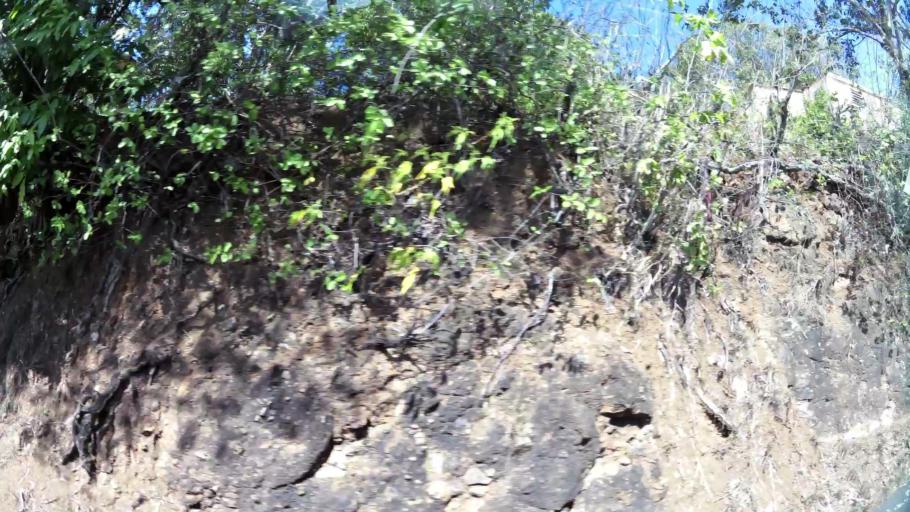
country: VG
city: Tortola
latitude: 18.4289
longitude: -64.6045
